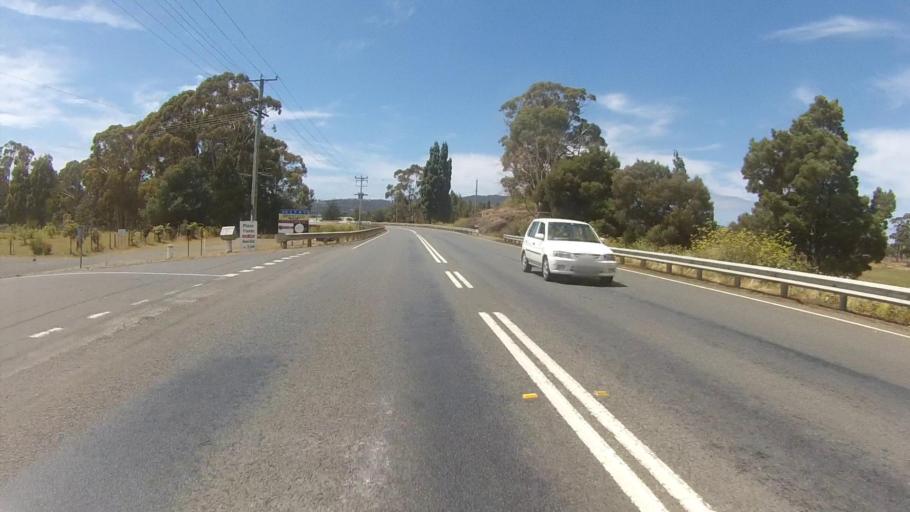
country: AU
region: Tasmania
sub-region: Kingborough
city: Margate
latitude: -43.0214
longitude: 147.2632
